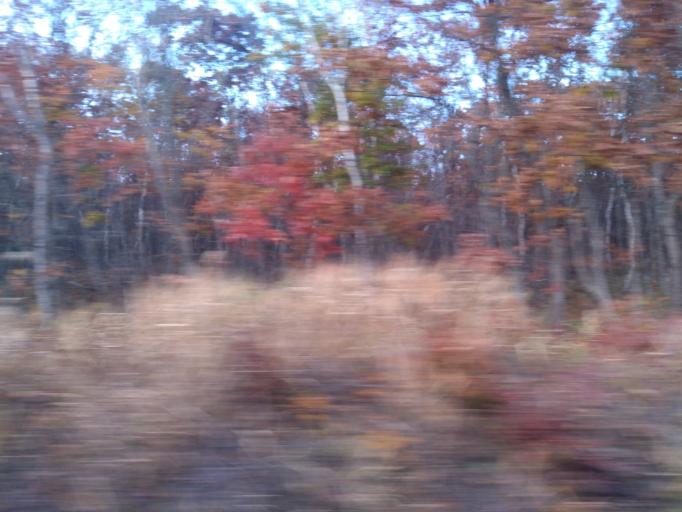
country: JP
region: Hokkaido
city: Tomakomai
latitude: 42.6885
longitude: 141.7255
